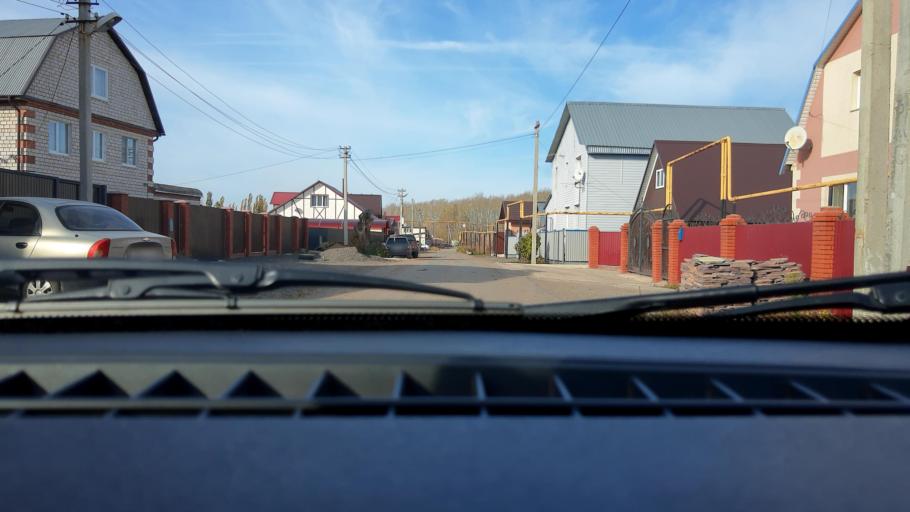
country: RU
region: Bashkortostan
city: Mikhaylovka
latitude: 54.7827
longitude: 55.9060
